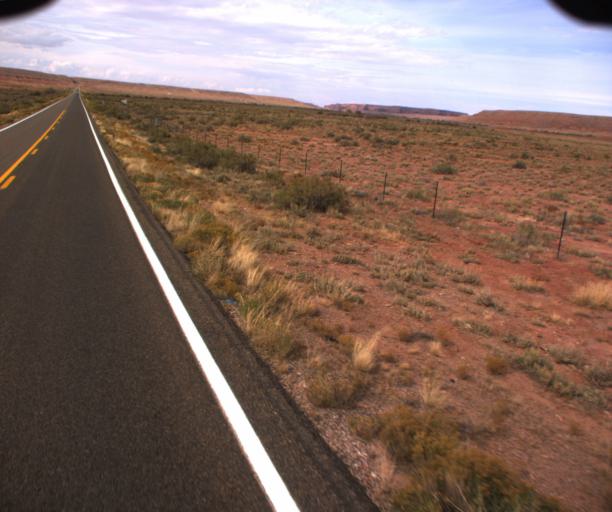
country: US
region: Arizona
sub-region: Apache County
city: Many Farms
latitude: 36.5265
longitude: -109.5004
